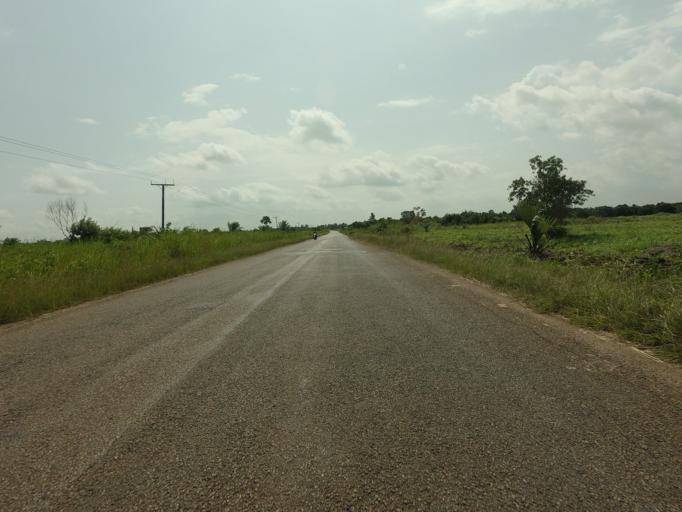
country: TG
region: Maritime
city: Lome
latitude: 6.2529
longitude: 0.9700
